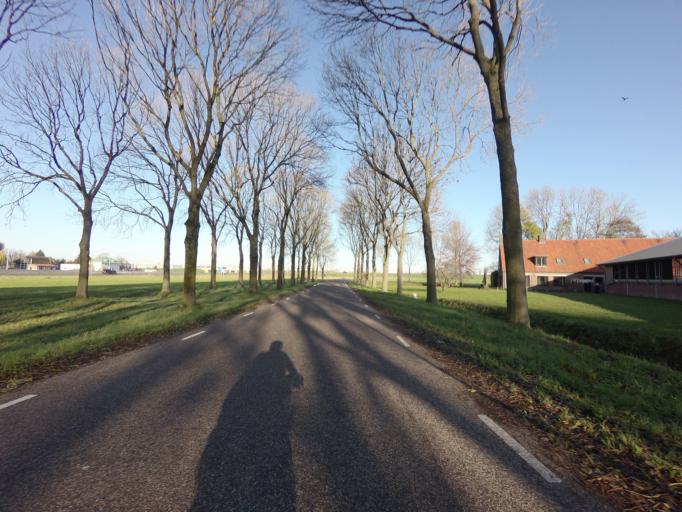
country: NL
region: Gelderland
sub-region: Gemeente Zaltbommel
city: Zaltbommel
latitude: 51.7899
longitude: 5.2594
